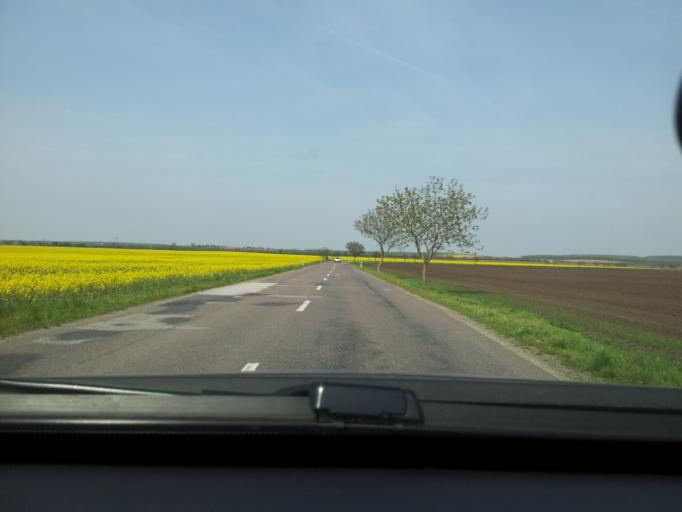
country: SK
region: Nitriansky
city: Tlmace
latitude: 48.2156
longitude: 18.5102
